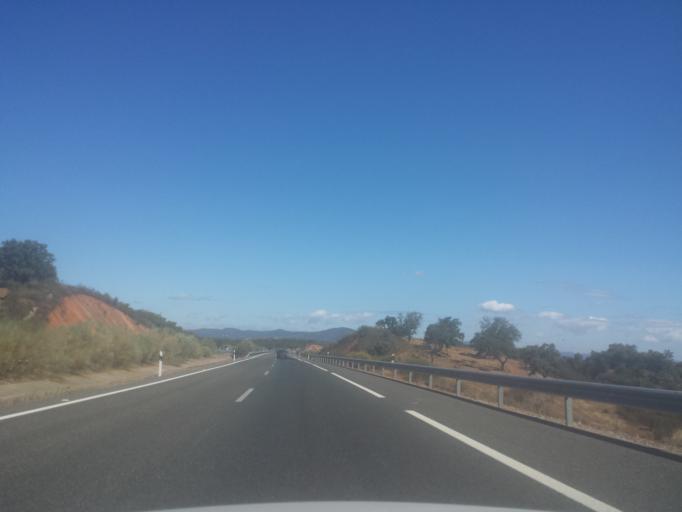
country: ES
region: Andalusia
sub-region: Provincia de Huelva
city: Santa Olalla del Cala
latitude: 37.8247
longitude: -6.2147
